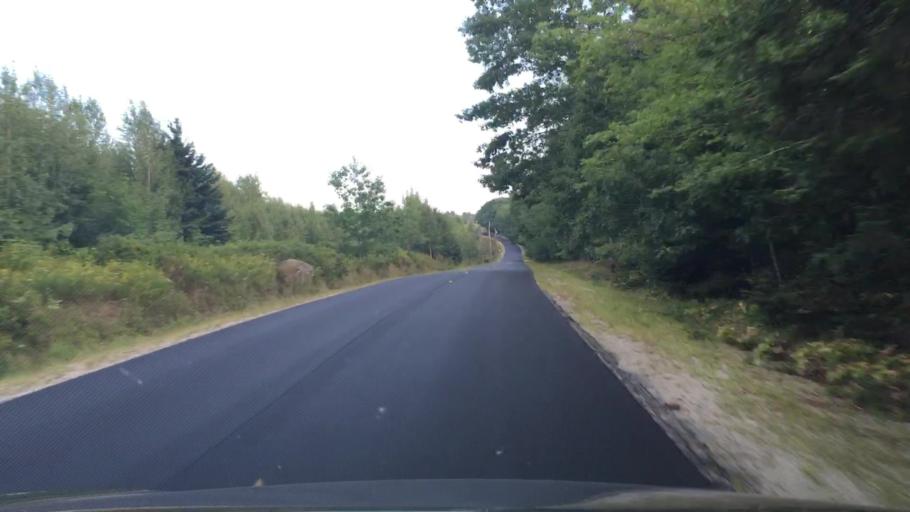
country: US
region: Maine
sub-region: Hancock County
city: Penobscot
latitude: 44.5415
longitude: -68.6165
